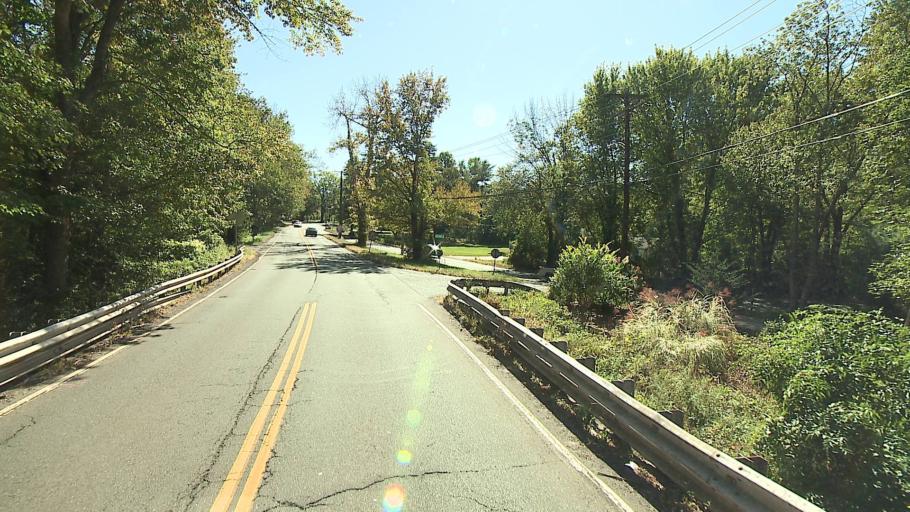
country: US
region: Connecticut
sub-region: New Haven County
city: Orange
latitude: 41.2591
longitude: -73.0514
